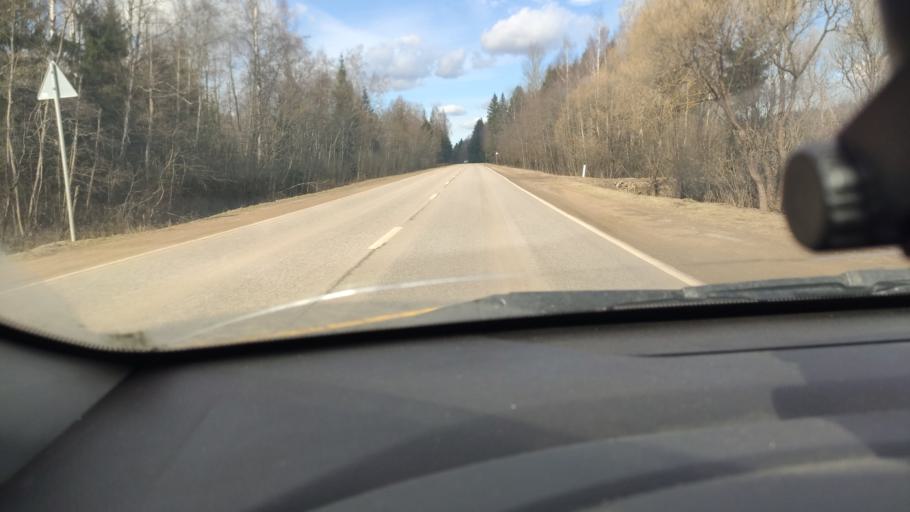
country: RU
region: Moskovskaya
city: Ruza
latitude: 55.7248
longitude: 36.1575
